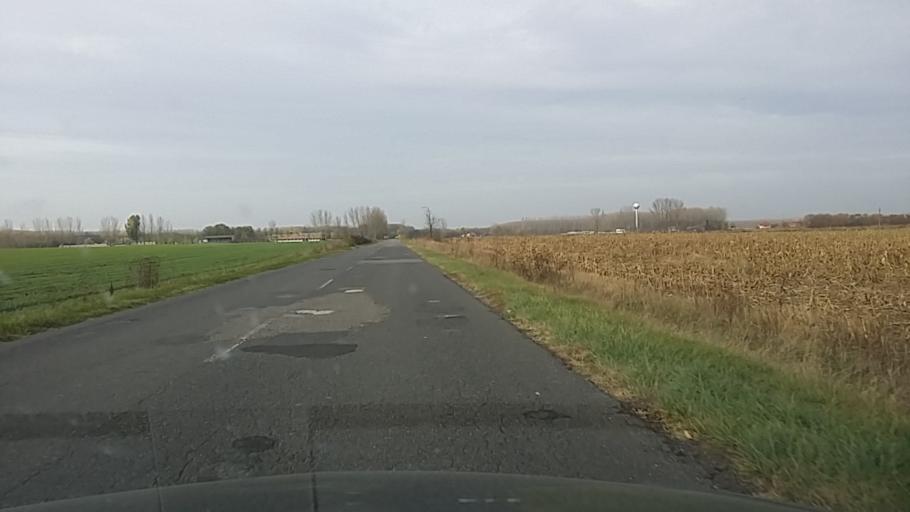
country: HU
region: Szabolcs-Szatmar-Bereg
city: Nyirbogdany
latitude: 48.0535
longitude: 21.8613
